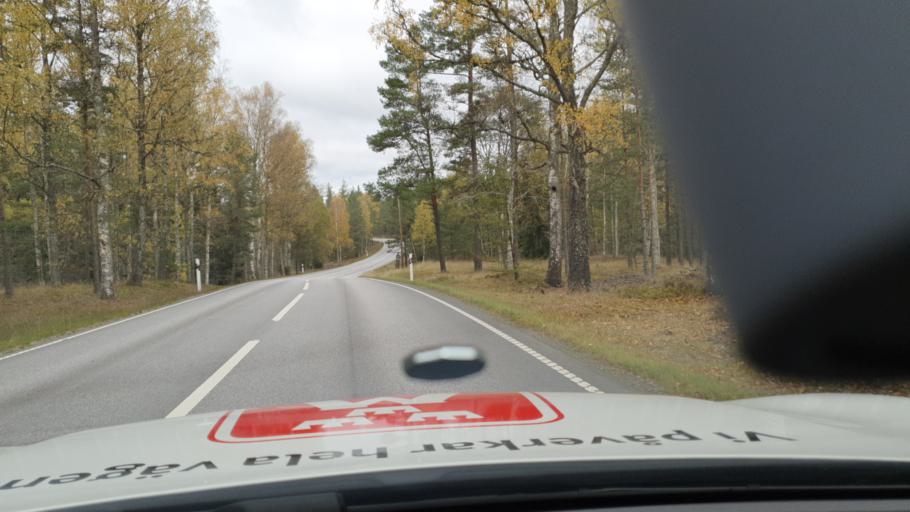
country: SE
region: OErebro
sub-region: Hallsbergs Kommun
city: Palsboda
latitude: 58.8427
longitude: 15.4032
